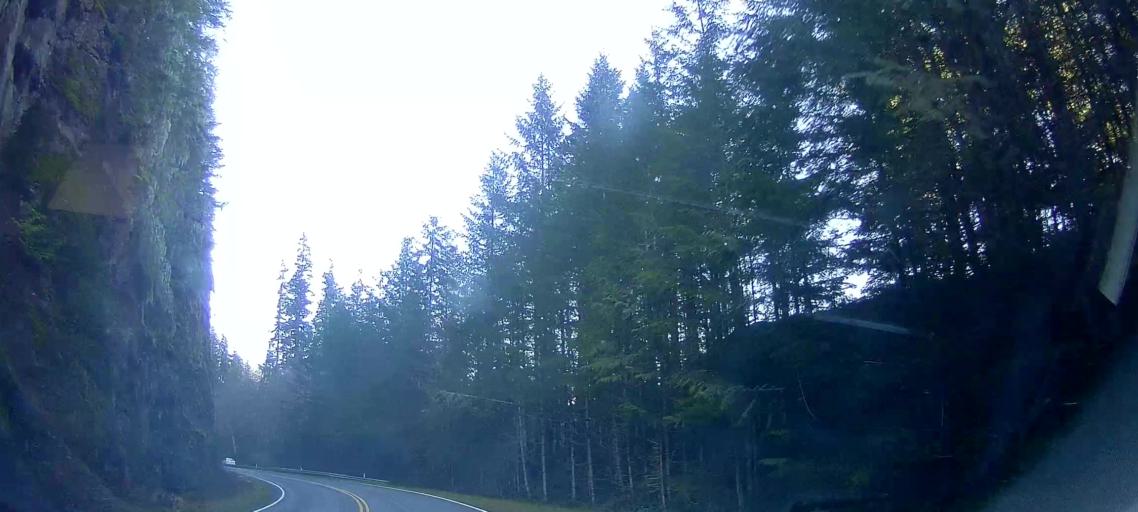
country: US
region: Washington
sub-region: Snohomish County
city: Darrington
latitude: 48.6529
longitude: -121.7102
